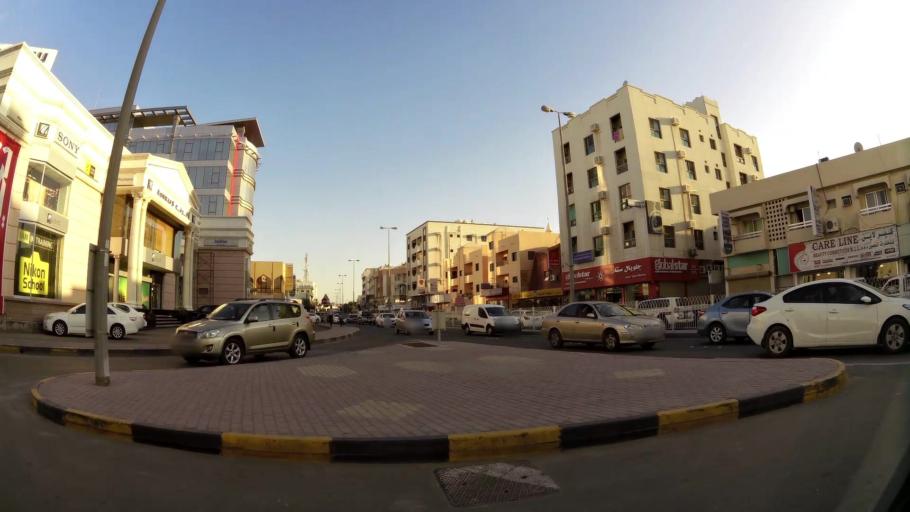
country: BH
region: Manama
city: Manama
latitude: 26.2353
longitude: 50.5881
